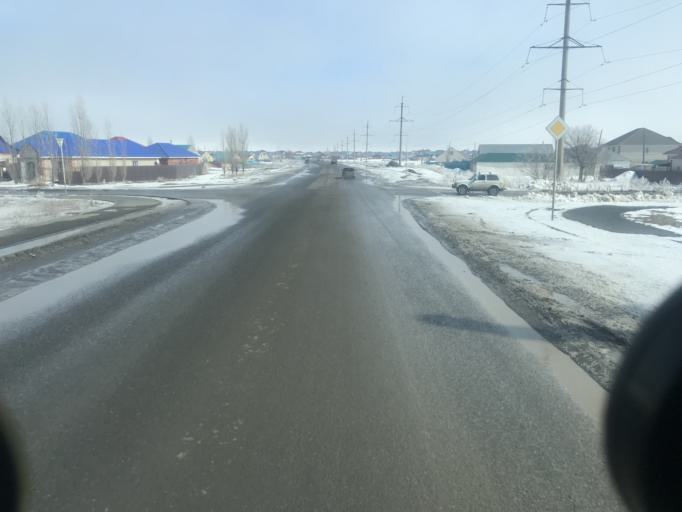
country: KZ
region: Aqtoebe
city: Aqtobe
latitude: 50.2764
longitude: 57.2723
